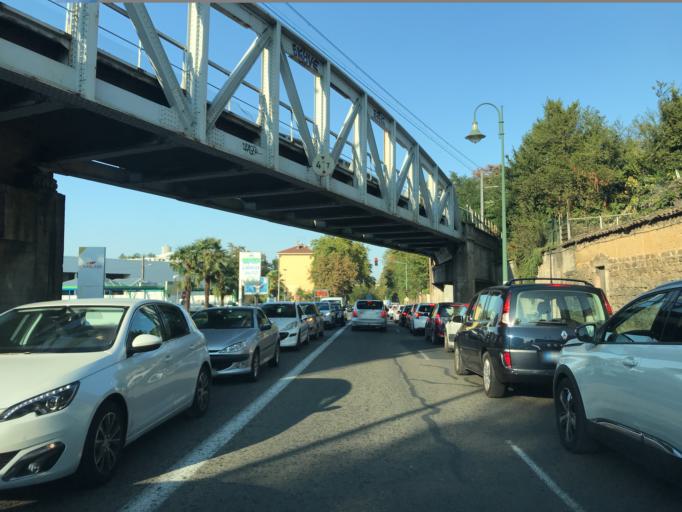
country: FR
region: Rhone-Alpes
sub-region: Departement du Rhone
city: Tassin-la-Demi-Lune
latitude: 45.7682
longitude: 4.7864
